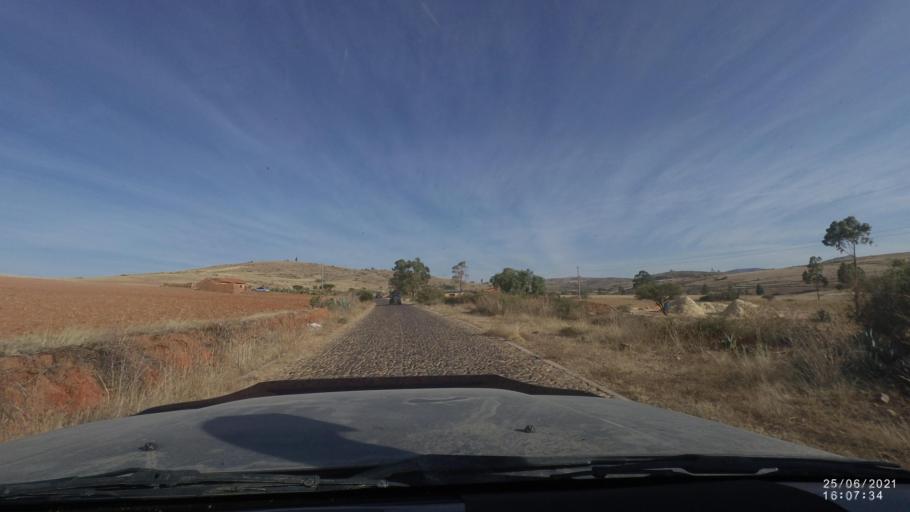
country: BO
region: Cochabamba
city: Cliza
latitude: -17.6752
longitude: -65.9040
